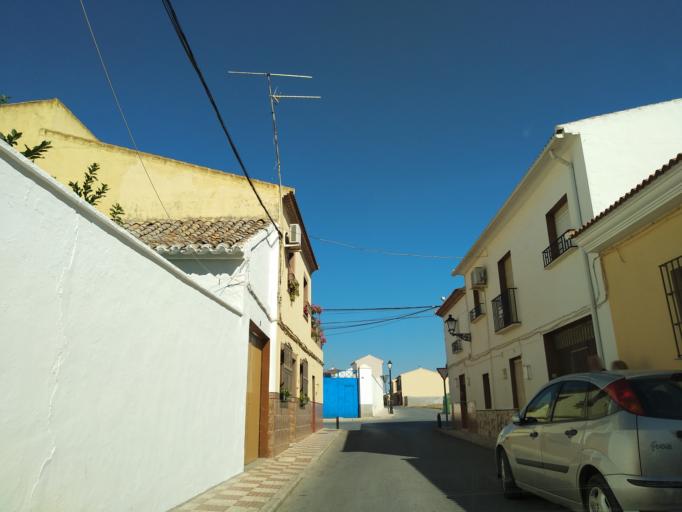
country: ES
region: Andalusia
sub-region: Provincia de Malaga
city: Mollina
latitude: 37.1288
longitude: -4.6565
